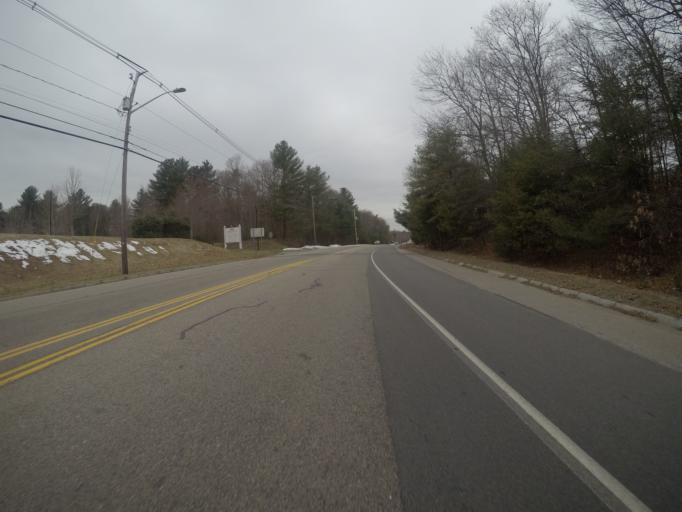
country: US
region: Massachusetts
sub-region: Bristol County
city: Easton
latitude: 42.0234
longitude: -71.1433
